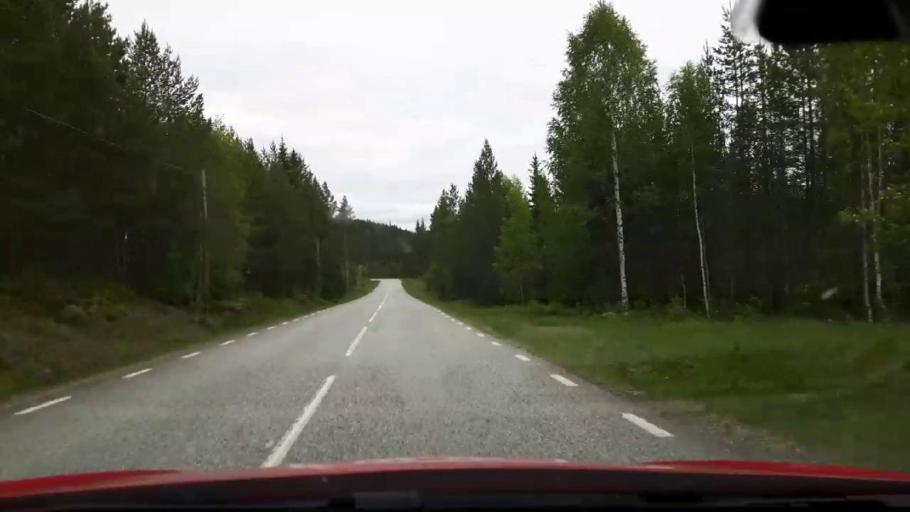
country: SE
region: Jaemtland
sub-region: Stroemsunds Kommun
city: Stroemsund
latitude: 63.3558
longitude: 15.7185
